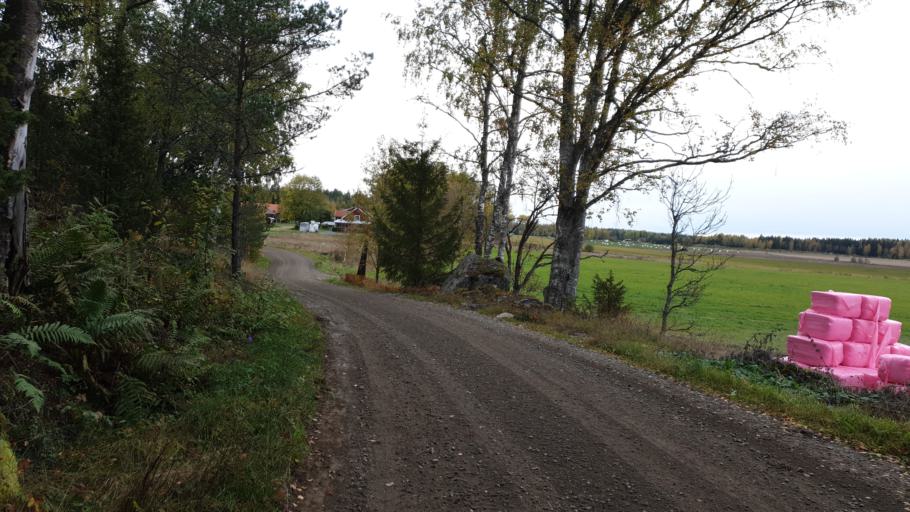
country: SE
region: Vaestmanland
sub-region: Sala Kommun
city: Sala
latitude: 59.8165
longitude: 16.6578
